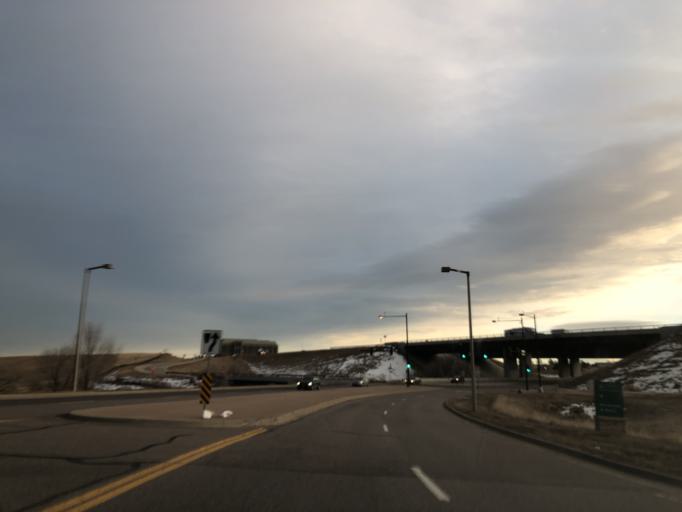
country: US
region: Colorado
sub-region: Douglas County
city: Meridian
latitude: 39.5559
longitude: -104.8625
